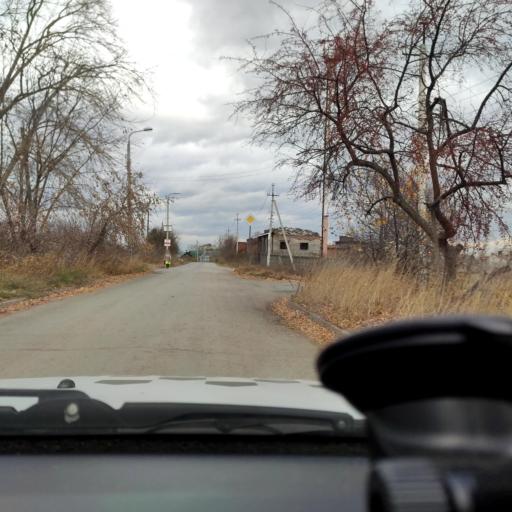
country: RU
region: Perm
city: Perm
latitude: 57.9943
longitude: 56.3376
